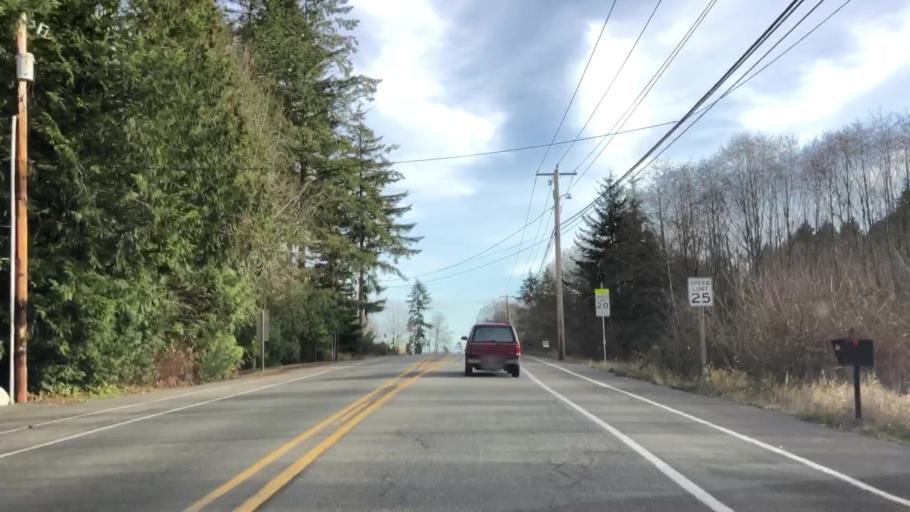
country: US
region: Washington
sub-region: Kitsap County
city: Kingston
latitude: 47.7950
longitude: -122.5189
